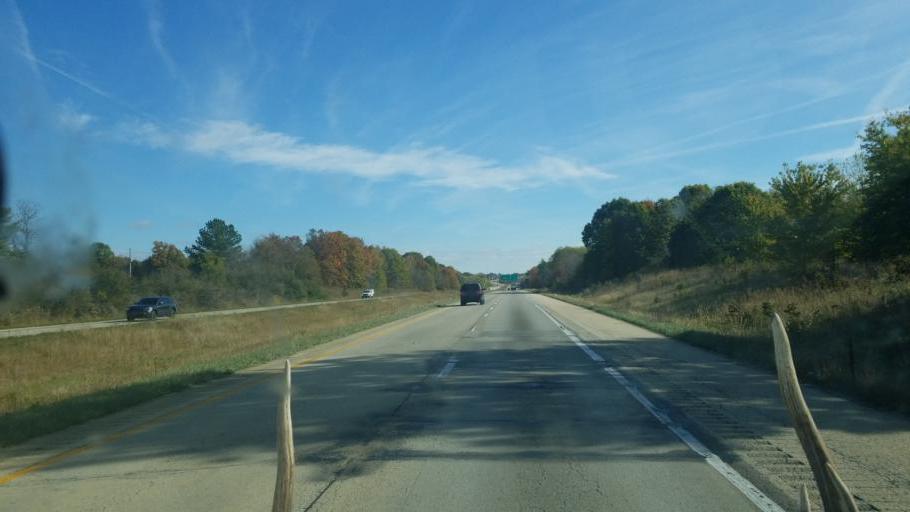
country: US
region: Illinois
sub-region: Effingham County
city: Effingham
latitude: 39.0867
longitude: -88.6071
